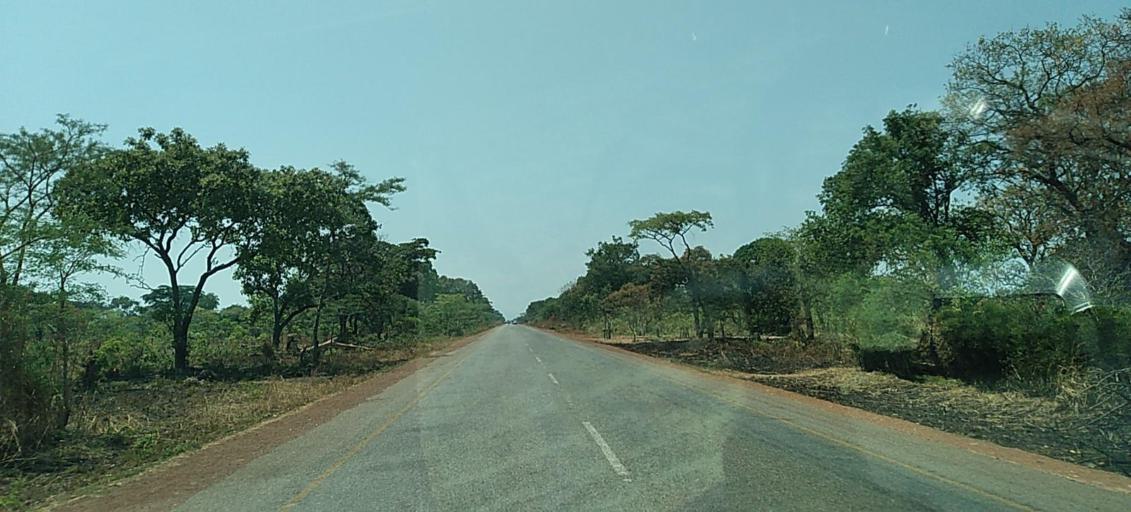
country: ZM
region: North-Western
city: Solwezi
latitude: -12.3835
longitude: 26.1964
